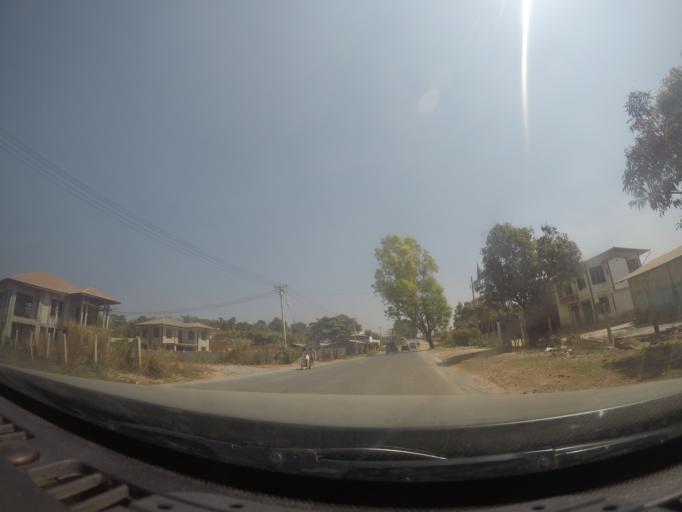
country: MM
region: Shan
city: Taunggyi
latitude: 20.7806
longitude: 97.1515
